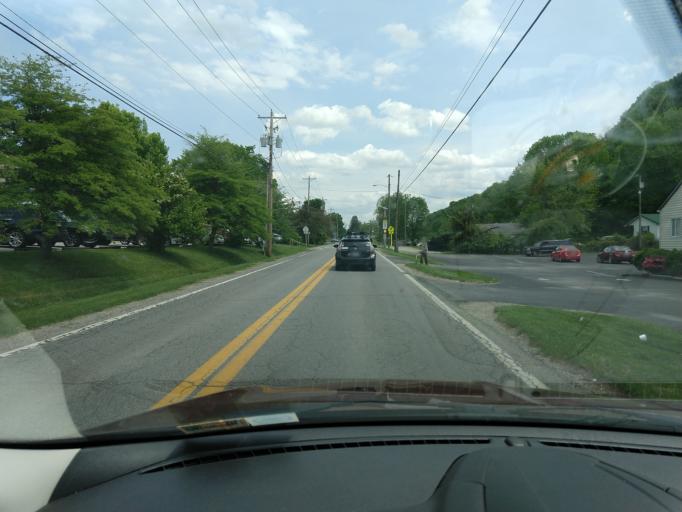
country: US
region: West Virginia
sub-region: Kanawha County
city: Cross Lanes
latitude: 38.3752
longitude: -81.7911
